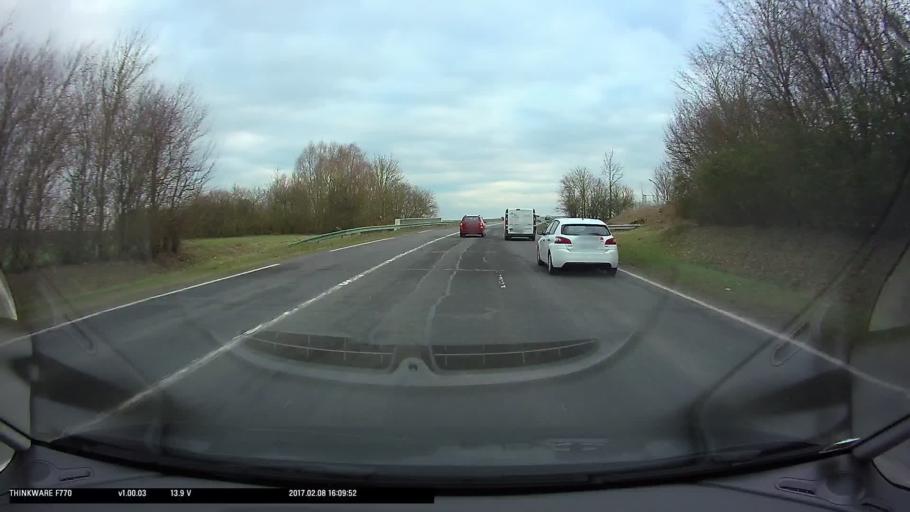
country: FR
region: Ile-de-France
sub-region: Departement du Val-d'Oise
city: Marines
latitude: 49.1208
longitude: 2.0271
